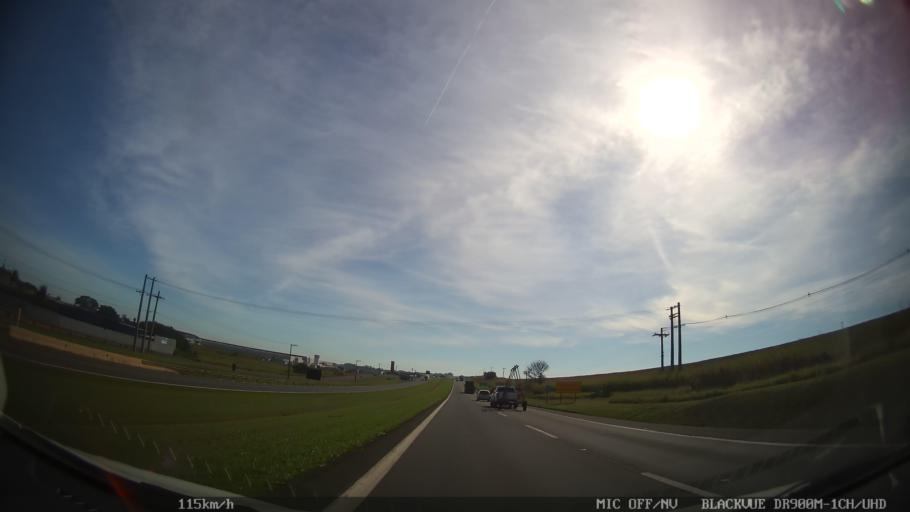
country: BR
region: Sao Paulo
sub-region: Cordeiropolis
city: Cordeiropolis
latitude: -22.4971
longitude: -47.3993
